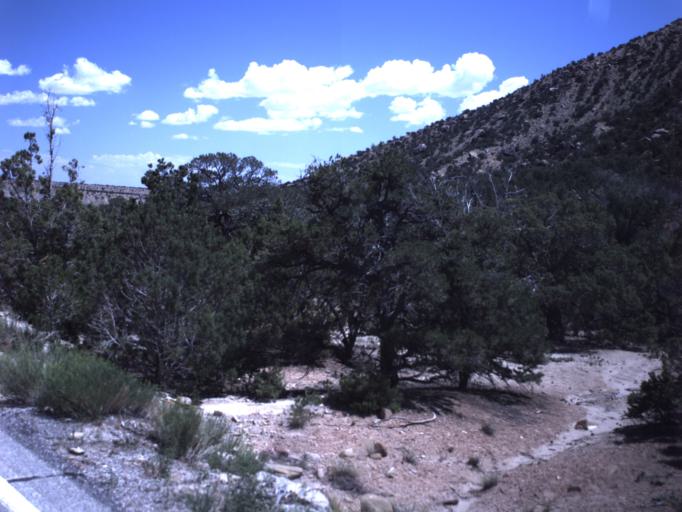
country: US
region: Utah
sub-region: Emery County
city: Orangeville
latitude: 39.2758
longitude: -111.1837
